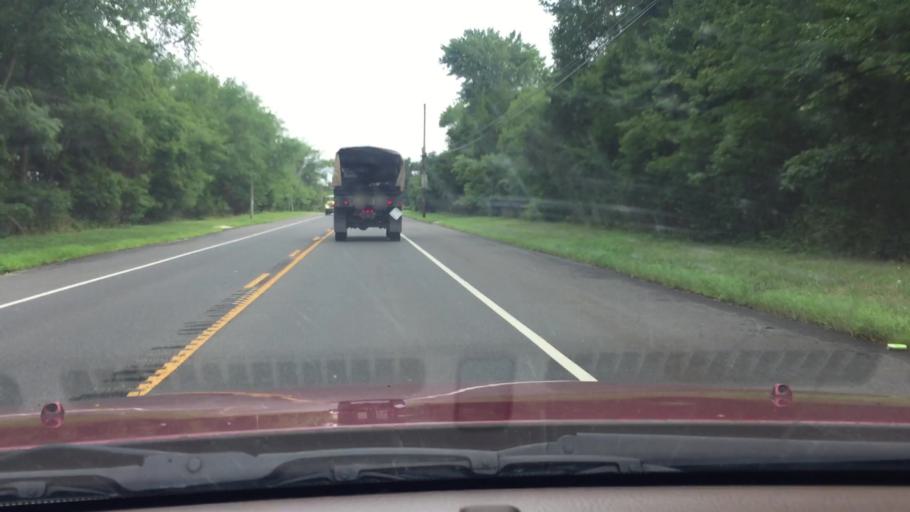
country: US
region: New Jersey
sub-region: Burlington County
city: Fort Dix
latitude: 40.0413
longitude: -74.6449
